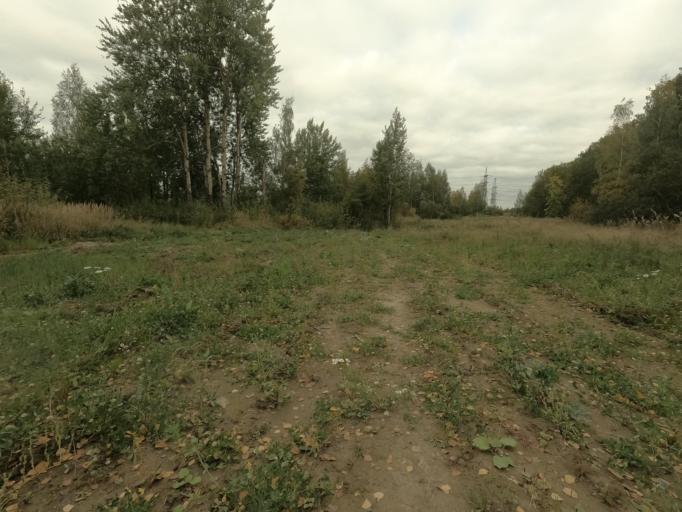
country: RU
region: St.-Petersburg
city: Metallostroy
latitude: 59.8164
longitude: 30.5429
